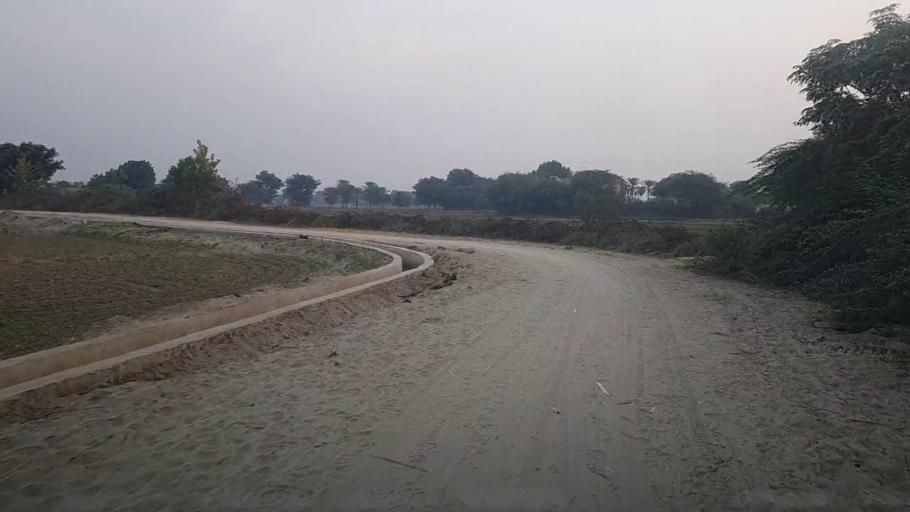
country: PK
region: Sindh
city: Kot Diji
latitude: 27.3463
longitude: 68.6357
